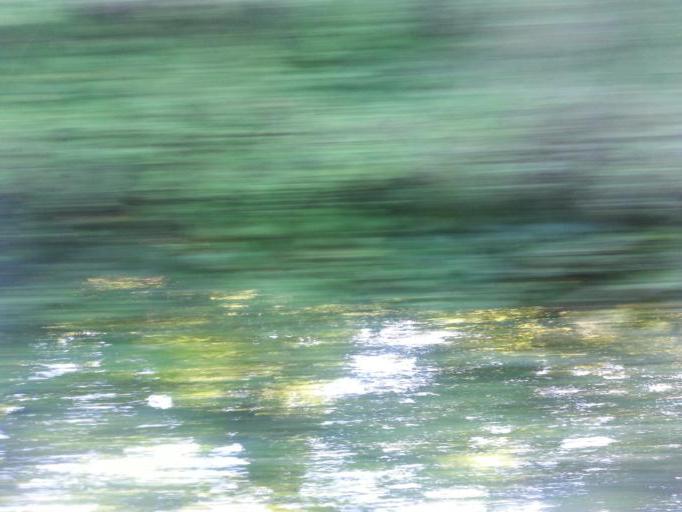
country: US
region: Tennessee
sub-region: Blount County
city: Maryville
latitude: 35.7055
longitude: -83.9055
